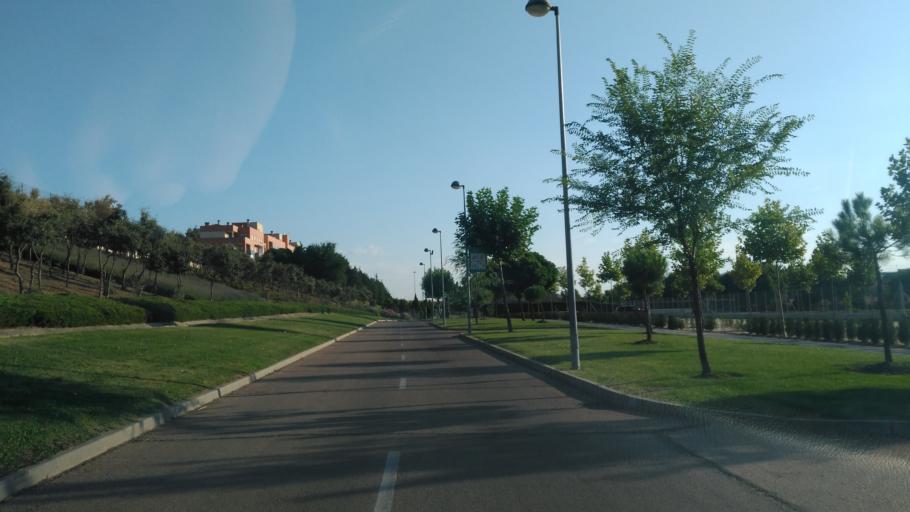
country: ES
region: Castille and Leon
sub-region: Provincia de Salamanca
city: Carbajosa de la Sagrada
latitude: 40.9407
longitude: -5.6483
